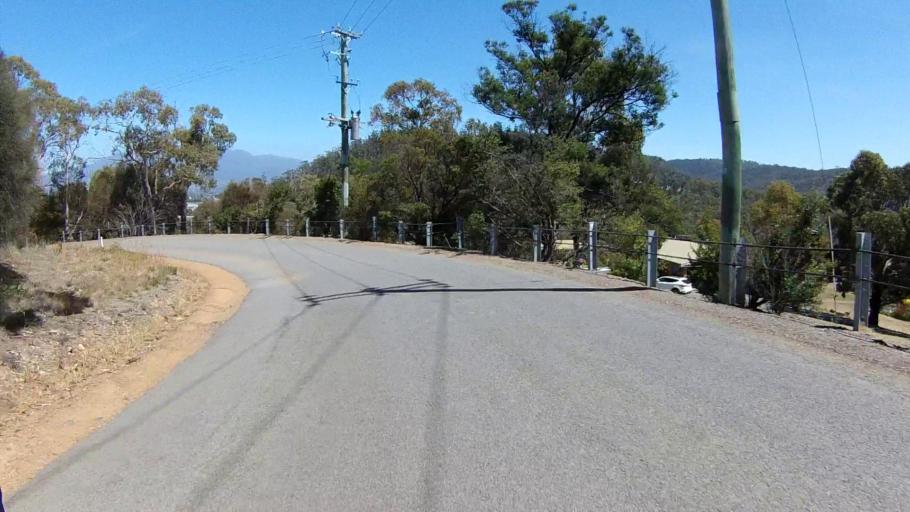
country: AU
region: Tasmania
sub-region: Clarence
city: Cambridge
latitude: -42.8537
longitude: 147.4238
